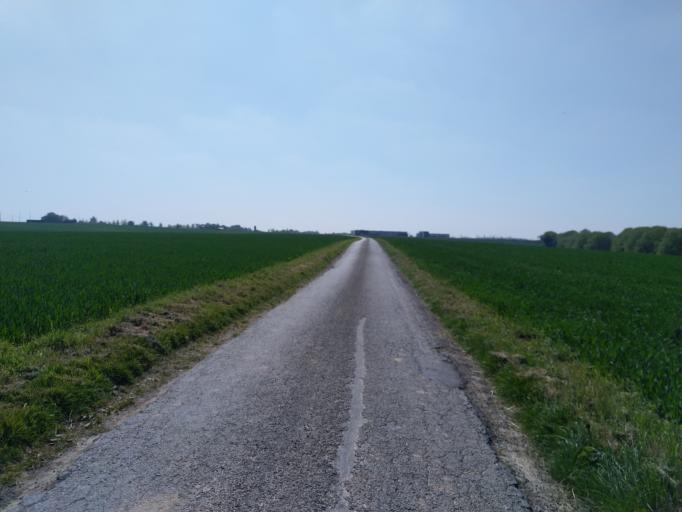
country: BE
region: Wallonia
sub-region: Province du Hainaut
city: Soignies
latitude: 50.5986
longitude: 4.0965
